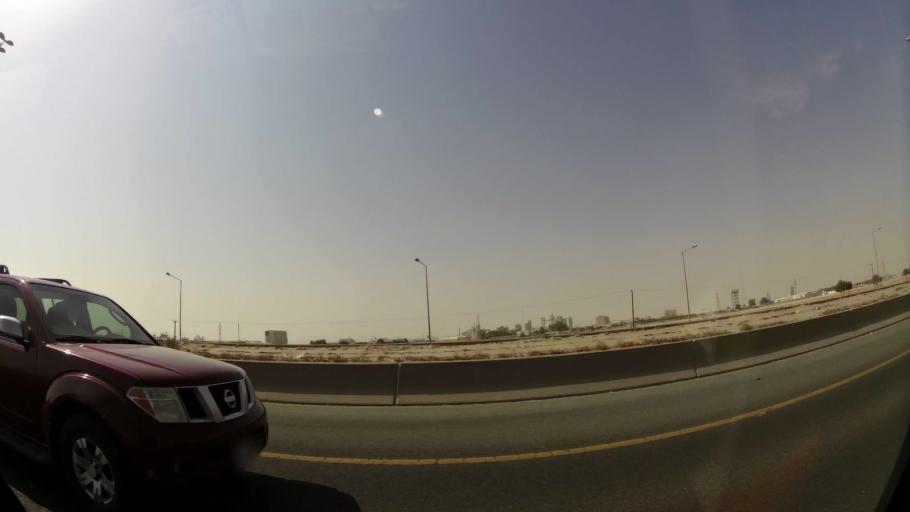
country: KW
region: Al Ahmadi
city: Al Fahahil
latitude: 29.0152
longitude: 48.1304
